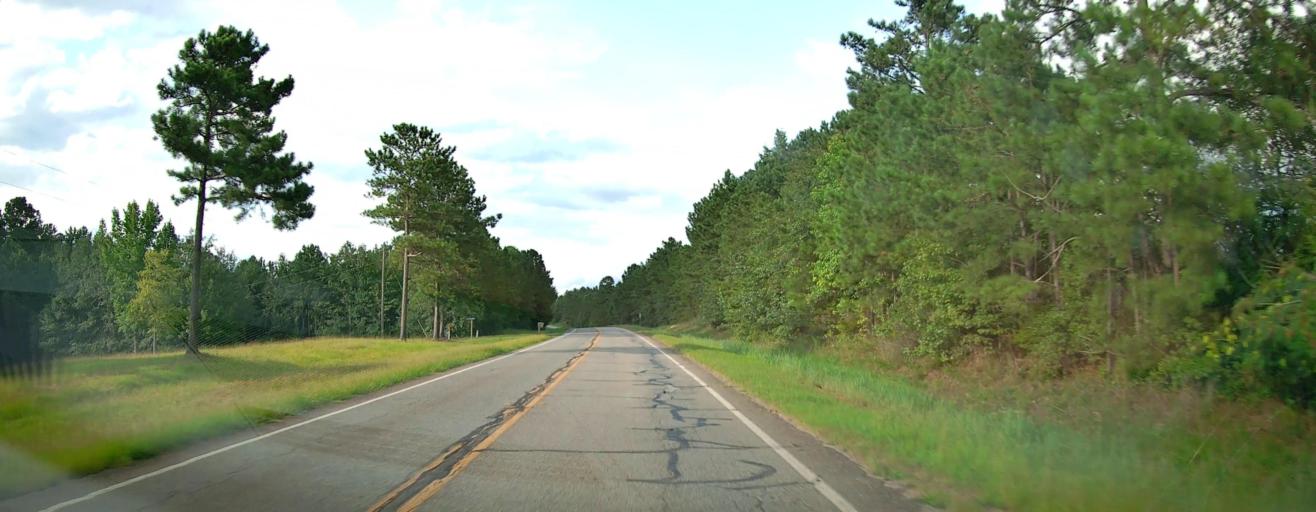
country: US
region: Georgia
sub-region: Crawford County
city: Roberta
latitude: 32.8141
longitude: -84.0248
